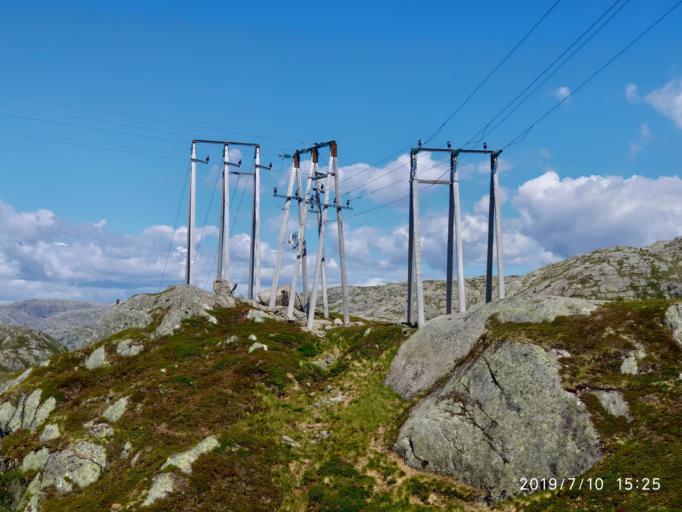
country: NO
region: Vest-Agder
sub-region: Sirdal
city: Tonstad
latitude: 59.0387
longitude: 6.7095
